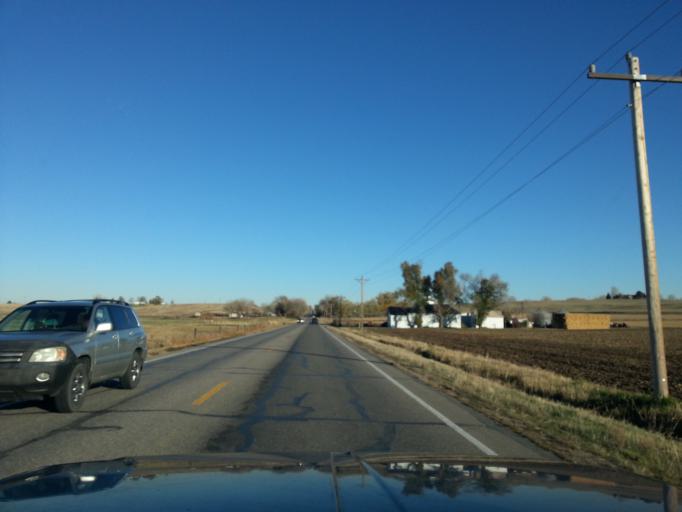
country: US
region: Colorado
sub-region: Larimer County
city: Loveland
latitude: 40.3783
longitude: -105.0350
